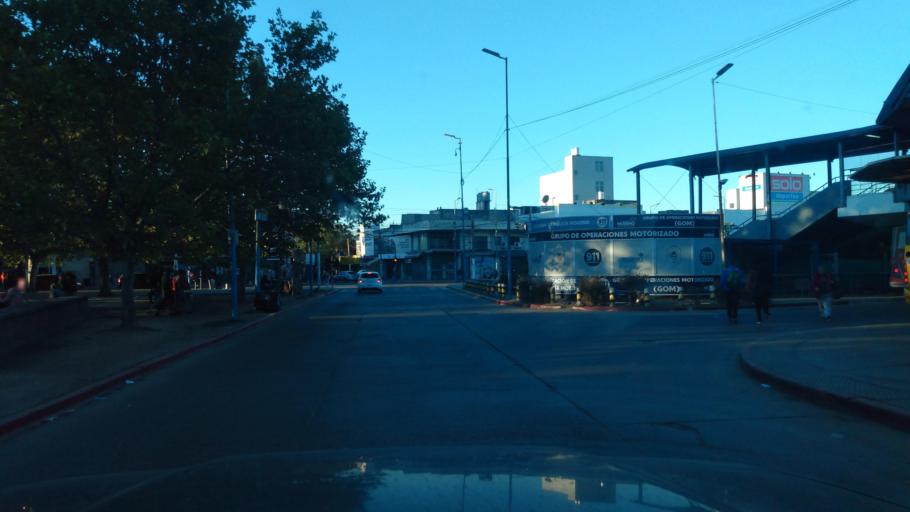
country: AR
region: Buenos Aires
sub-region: Partido de Merlo
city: Merlo
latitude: -34.6496
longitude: -58.7903
